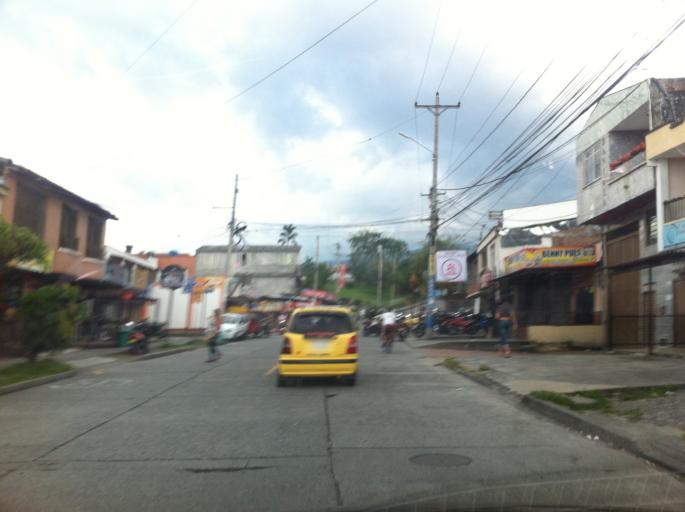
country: CO
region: Quindio
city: Armenia
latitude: 4.5220
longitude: -75.6899
